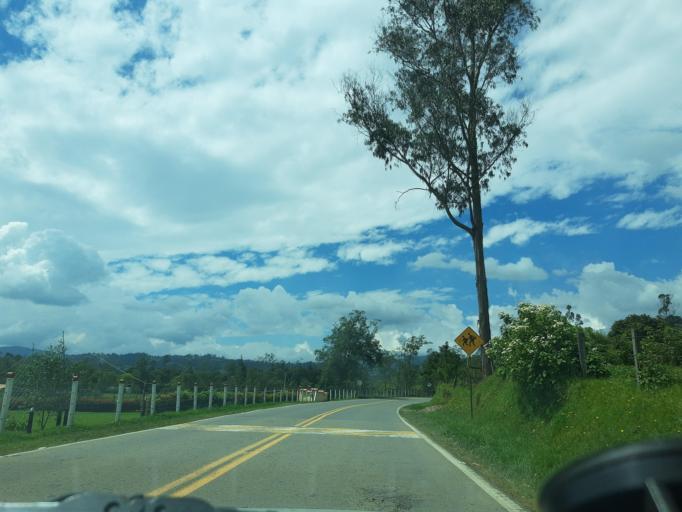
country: CO
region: Boyaca
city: Chiquinquira
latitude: 5.6137
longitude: -73.7423
